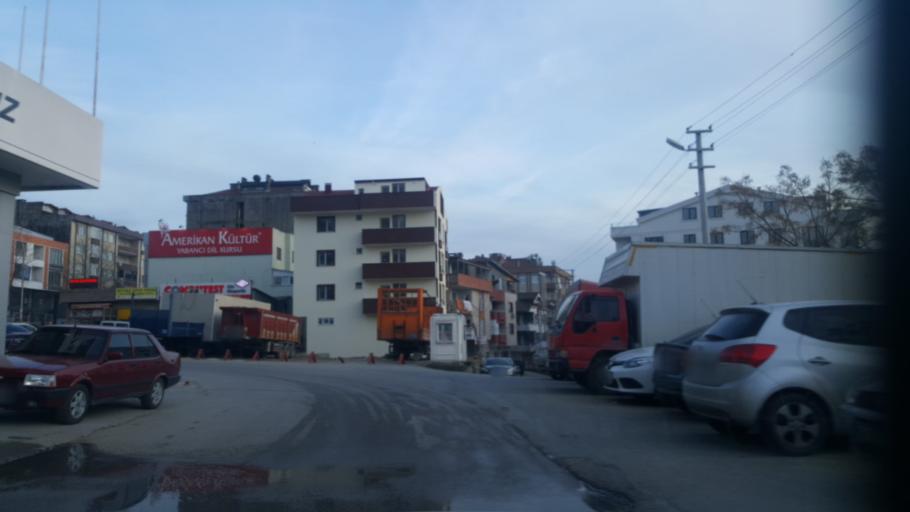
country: TR
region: Kocaeli
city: Gebze
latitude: 40.7936
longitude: 29.4328
